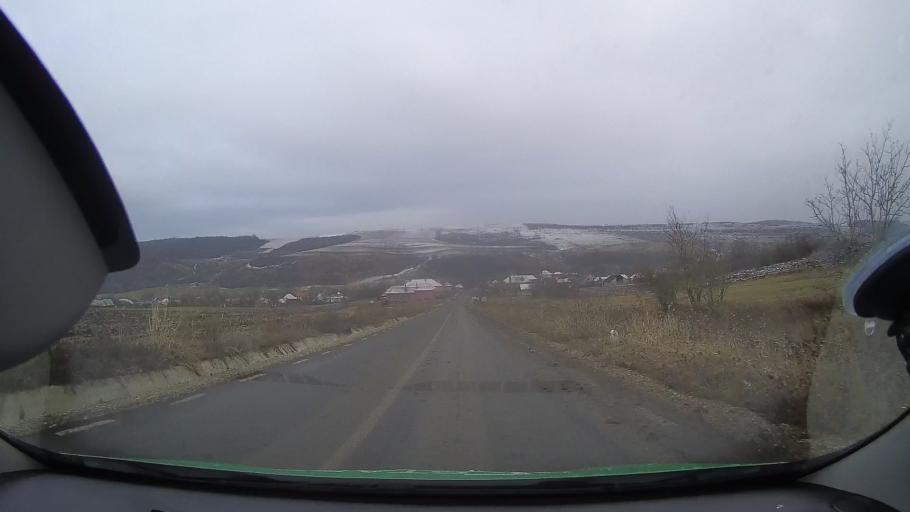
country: RO
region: Alba
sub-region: Comuna Farau
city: Farau
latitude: 46.3896
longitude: 24.0211
